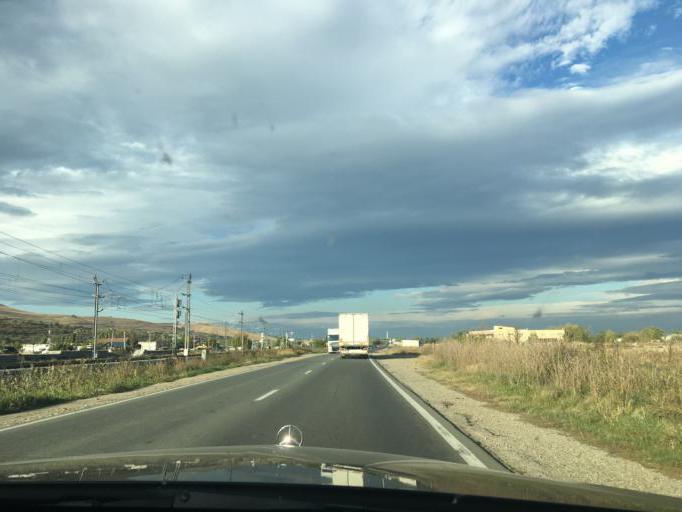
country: RO
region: Alba
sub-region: Municipiul Alba Iulia
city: Barabant
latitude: 46.0983
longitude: 23.6053
